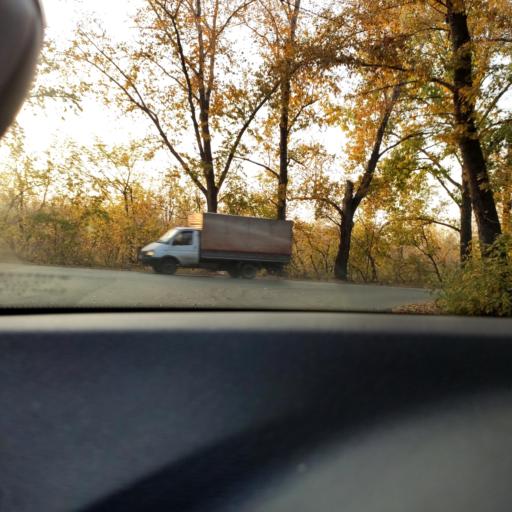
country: RU
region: Samara
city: Smyshlyayevka
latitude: 53.2511
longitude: 50.3688
